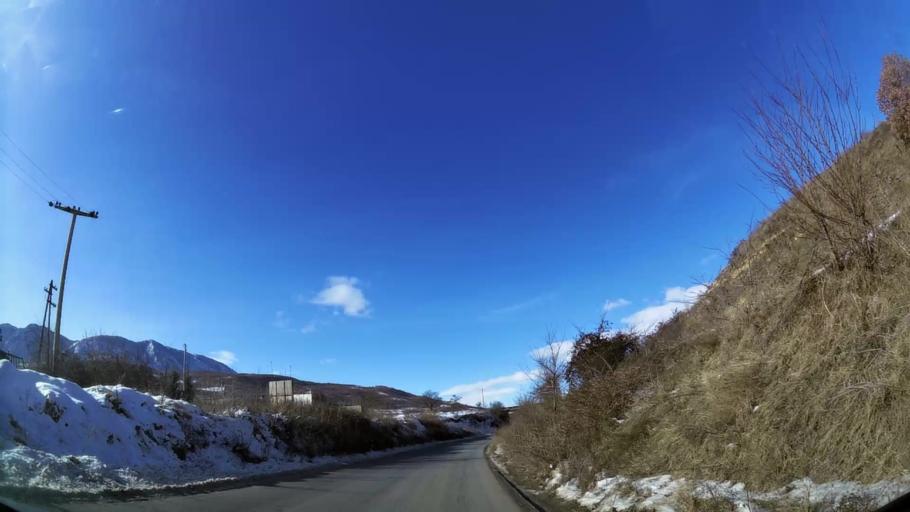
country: MK
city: Ljubin
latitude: 41.9855
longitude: 21.3055
